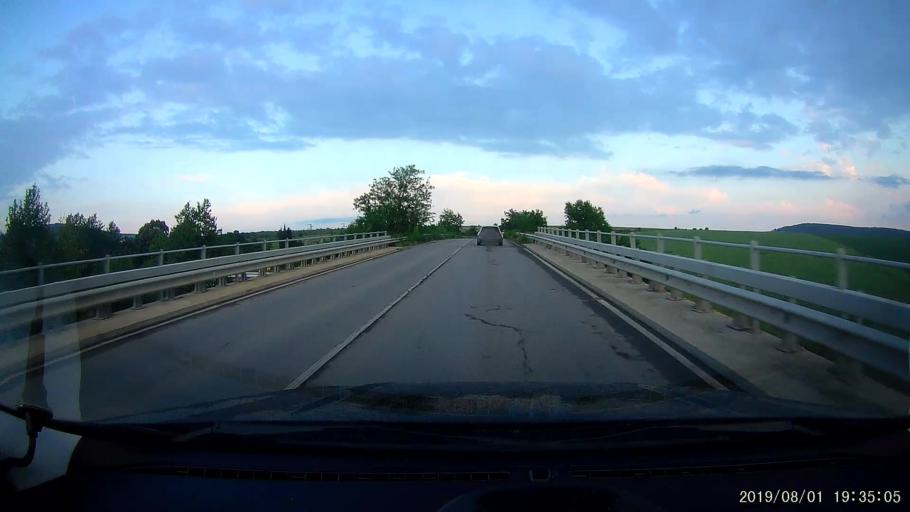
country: BG
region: Burgas
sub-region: Obshtina Sungurlare
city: Sungurlare
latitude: 42.7647
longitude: 26.8812
